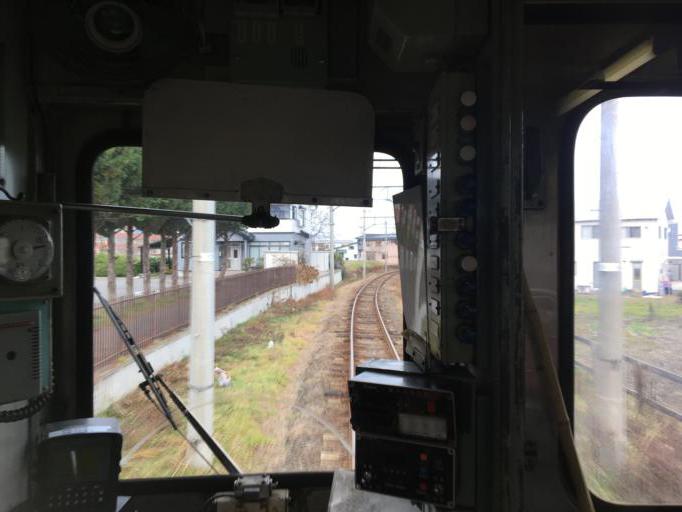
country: JP
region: Aomori
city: Hirosaki
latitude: 40.5732
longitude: 140.4742
